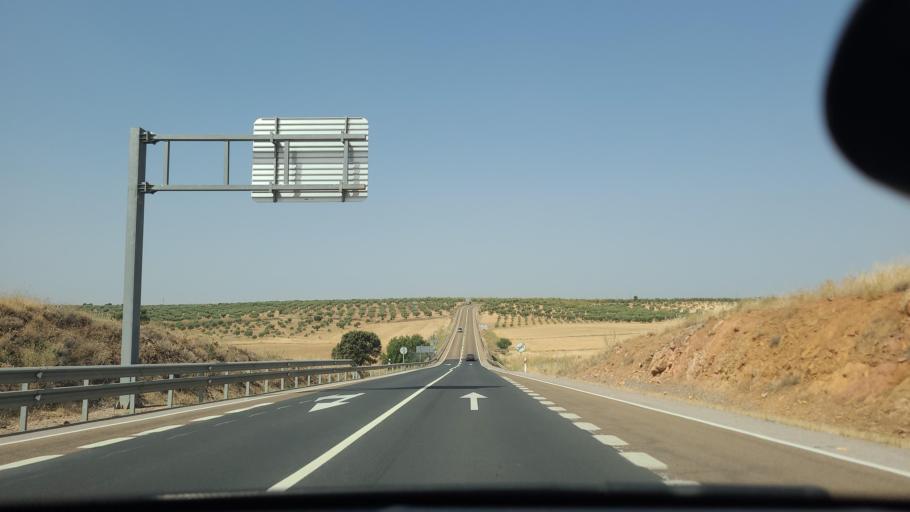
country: ES
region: Extremadura
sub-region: Provincia de Badajoz
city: Usagre
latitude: 38.3451
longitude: -6.1755
